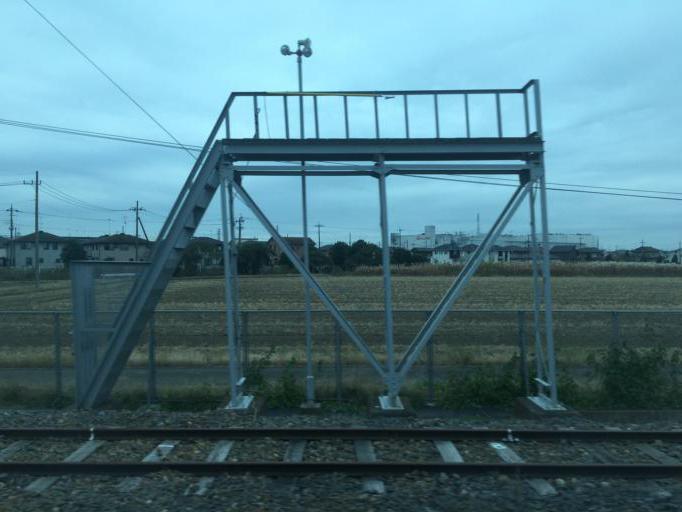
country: JP
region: Ibaraki
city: Shimodate
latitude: 36.3032
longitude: 139.9715
